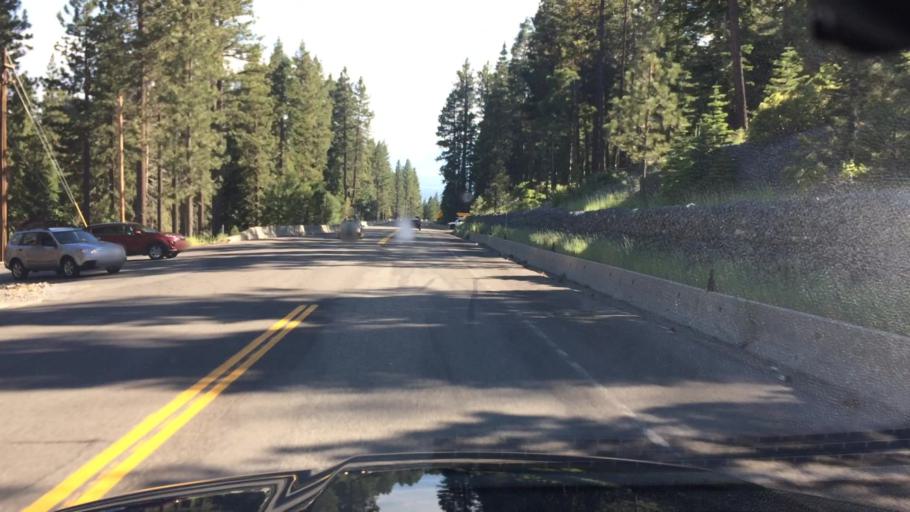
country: US
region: Nevada
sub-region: Washoe County
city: Incline Village
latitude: 39.2627
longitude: -119.9569
